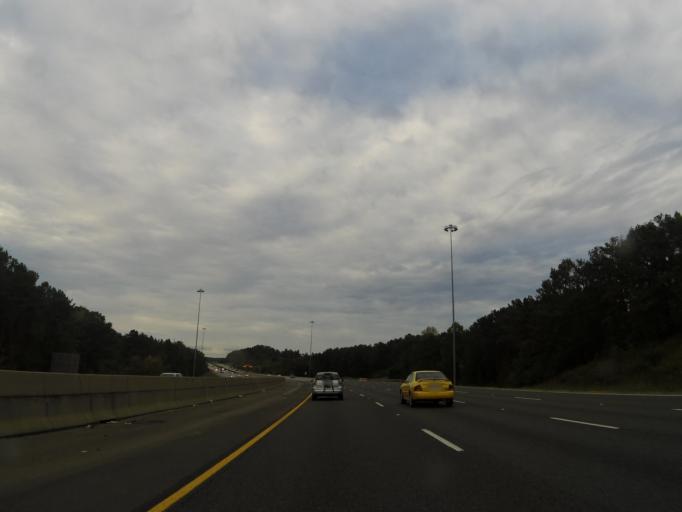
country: US
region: Alabama
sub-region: Shelby County
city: Indian Springs Village
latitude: 33.3651
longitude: -86.7763
